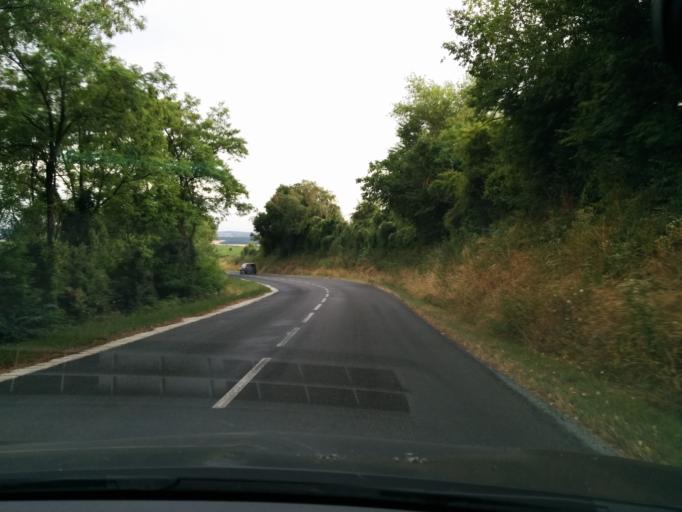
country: FR
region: Centre
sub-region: Departement du Cher
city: Sancerre
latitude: 47.3201
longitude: 2.7989
